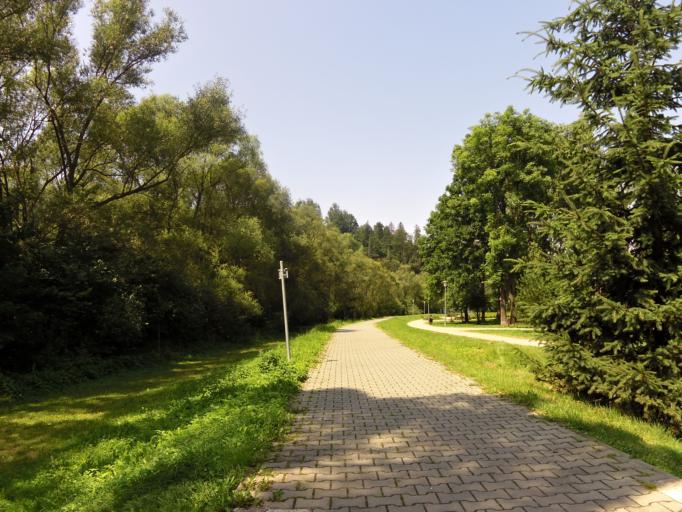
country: PL
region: Silesian Voivodeship
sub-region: Powiat zywiecki
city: Milowka
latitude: 49.5546
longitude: 19.0845
